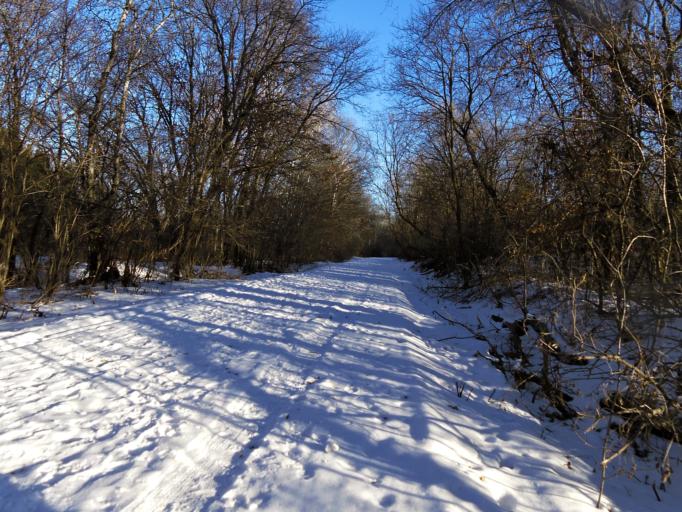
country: US
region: Minnesota
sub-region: Washington County
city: Grant
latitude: 45.0776
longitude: -92.8789
